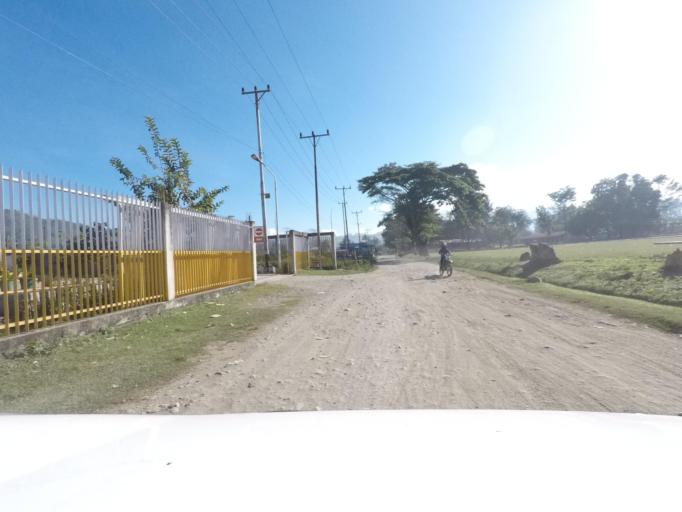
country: TL
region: Ermera
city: Gleno
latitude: -8.7237
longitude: 125.4313
